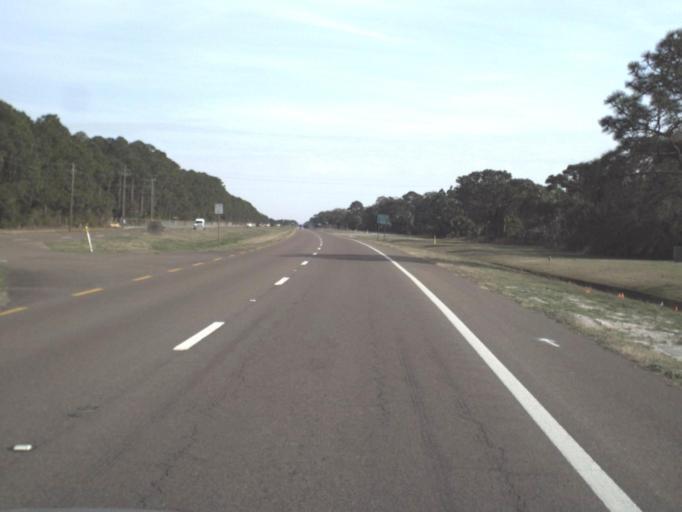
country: US
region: Florida
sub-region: Bay County
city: Tyndall Air Force Base
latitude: 30.0824
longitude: -85.6063
